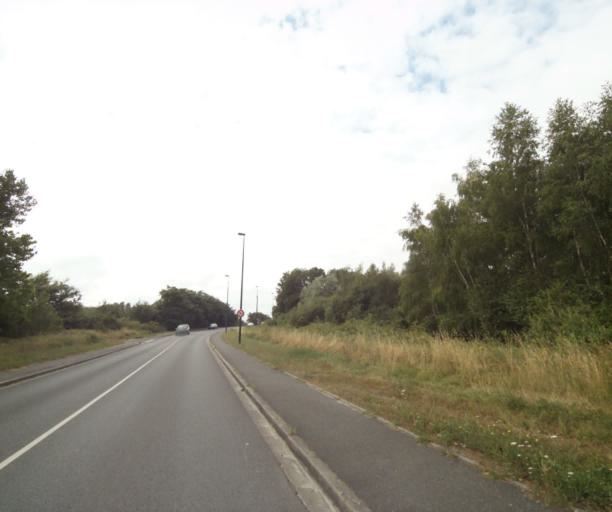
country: FR
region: Centre
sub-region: Departement du Loiret
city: Checy
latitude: 47.8978
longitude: 2.0411
